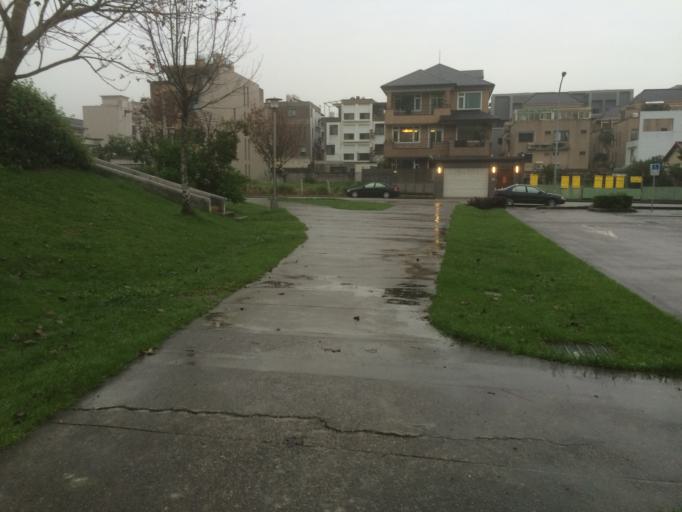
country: TW
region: Taiwan
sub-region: Taichung City
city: Taichung
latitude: 24.1788
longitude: 120.7150
